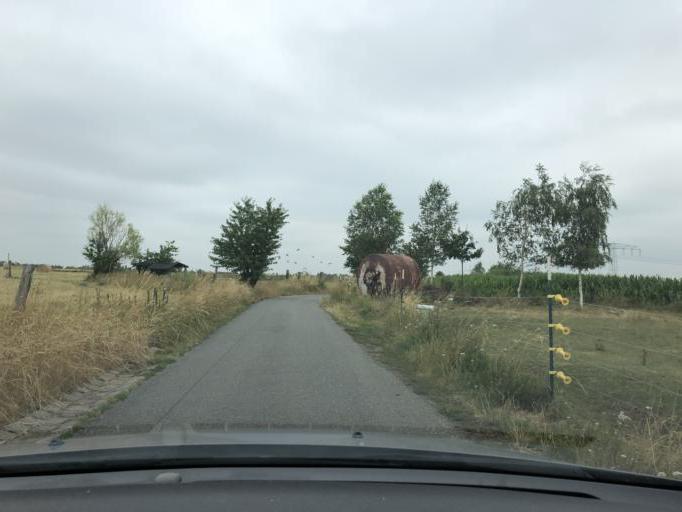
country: DE
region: Saxony
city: Frohburg
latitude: 51.1017
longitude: 12.5612
